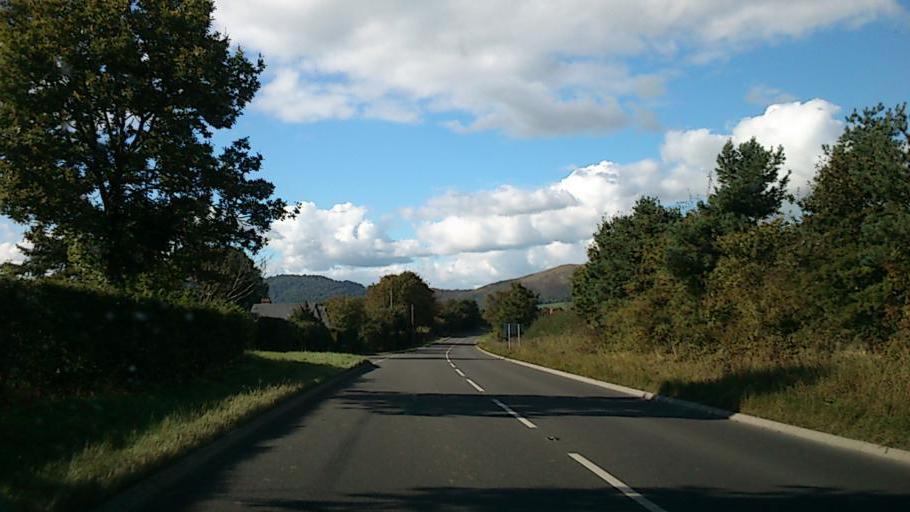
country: GB
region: England
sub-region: Shropshire
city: Westbury
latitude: 52.6985
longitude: -2.9850
